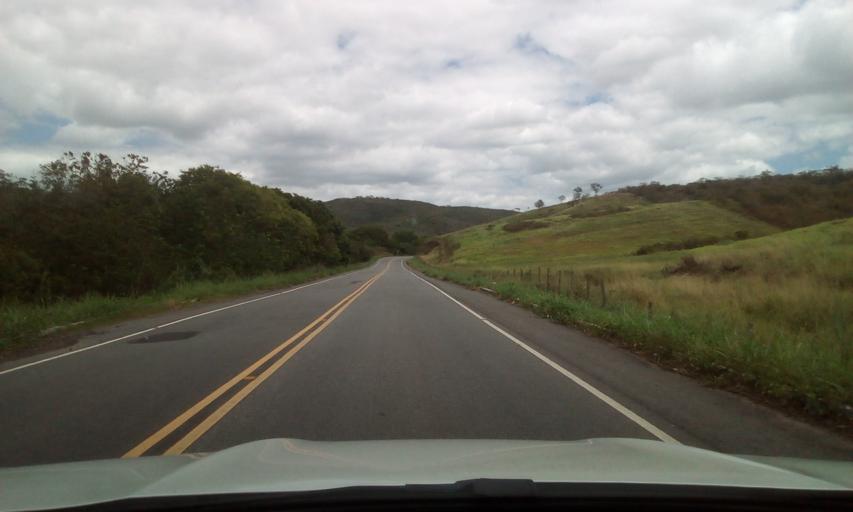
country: BR
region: Paraiba
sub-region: Serra Redonda
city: Alagoa Grande
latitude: -7.1563
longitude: -35.6053
